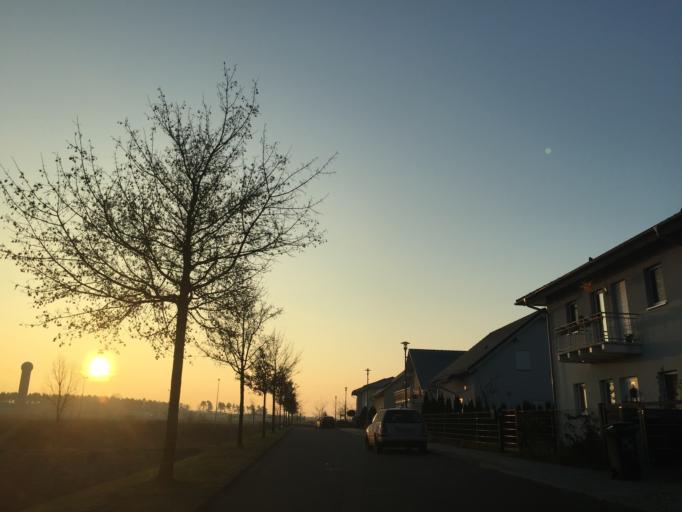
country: DE
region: Berlin
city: Kladow
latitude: 52.4751
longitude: 13.1321
